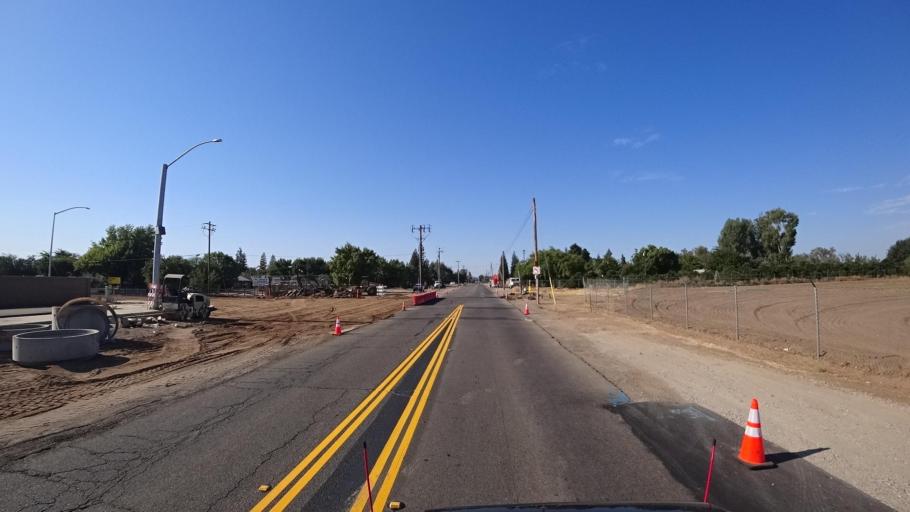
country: US
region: California
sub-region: Fresno County
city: Sunnyside
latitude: 36.7652
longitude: -119.6641
